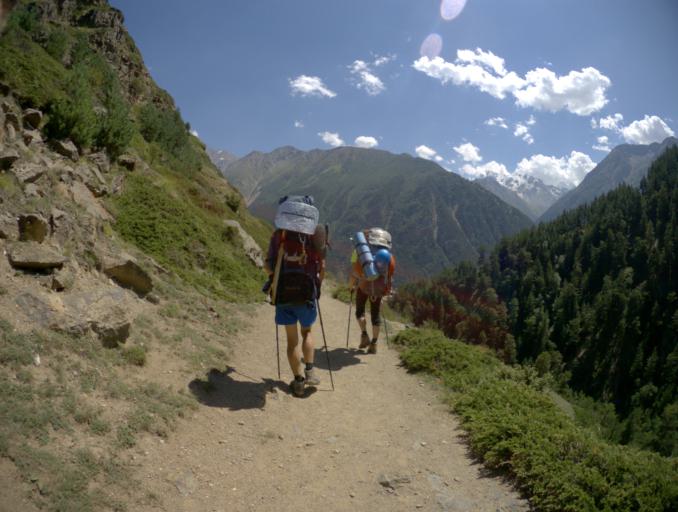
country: RU
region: Kabardino-Balkariya
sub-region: El'brusskiy Rayon
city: El'brus
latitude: 43.2638
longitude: 42.6366
